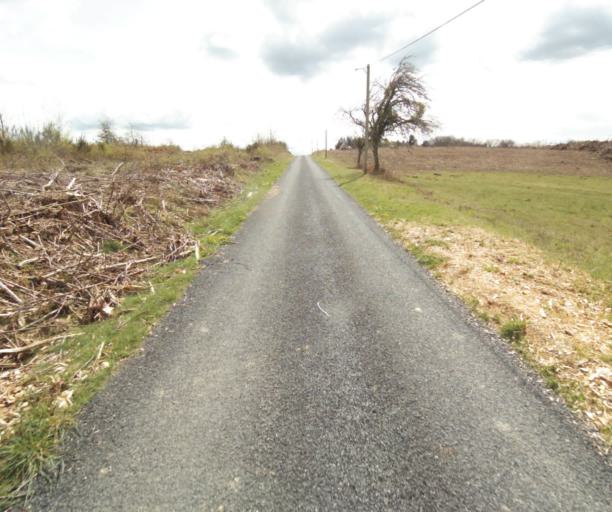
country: FR
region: Limousin
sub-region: Departement de la Correze
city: Laguenne
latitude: 45.2356
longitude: 1.8726
